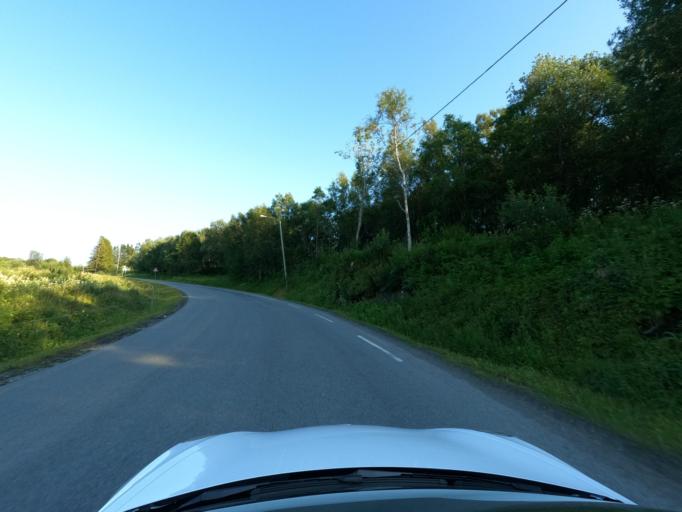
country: NO
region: Nordland
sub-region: Evenes
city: Randa
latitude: 68.4905
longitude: 16.8952
